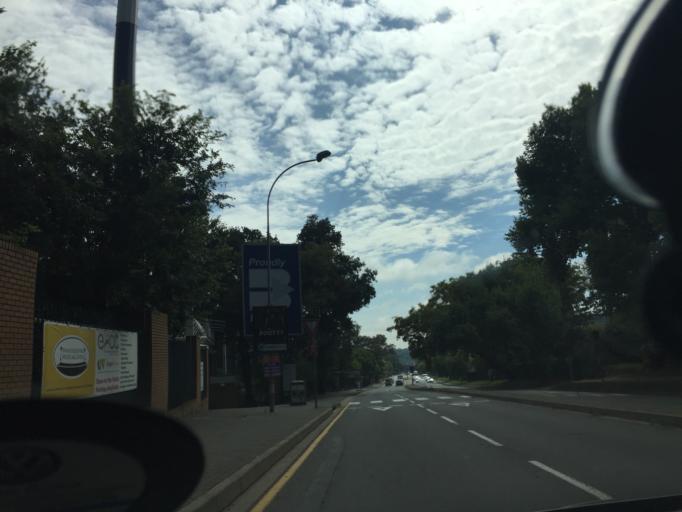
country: ZA
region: Gauteng
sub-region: City of Johannesburg Metropolitan Municipality
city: Johannesburg
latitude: -26.1325
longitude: 28.0576
